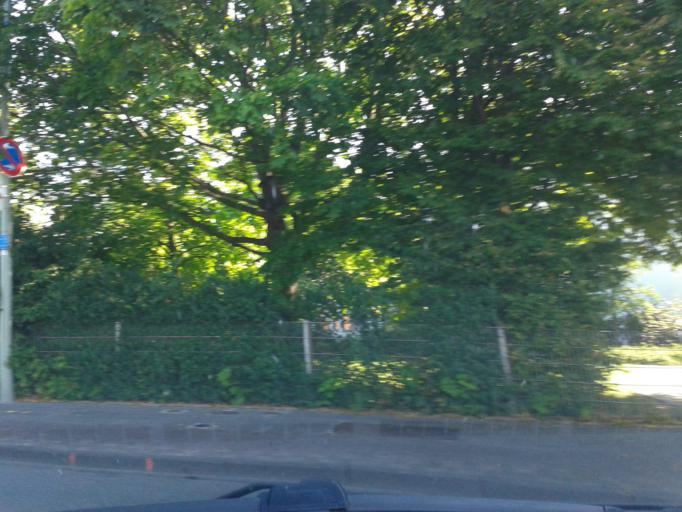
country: DE
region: North Rhine-Westphalia
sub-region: Regierungsbezirk Detmold
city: Paderborn
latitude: 51.7381
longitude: 8.6808
